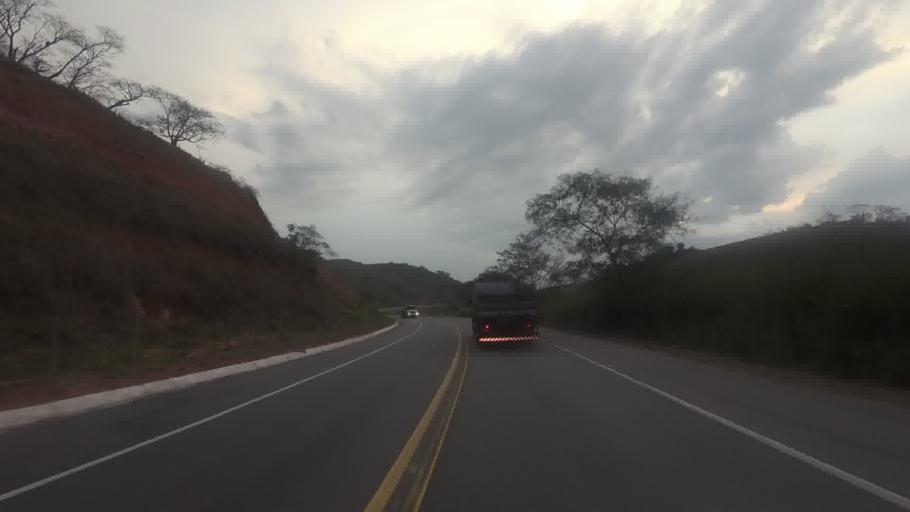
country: BR
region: Minas Gerais
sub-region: Alem Paraiba
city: Alem Paraiba
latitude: -21.8554
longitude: -42.6534
